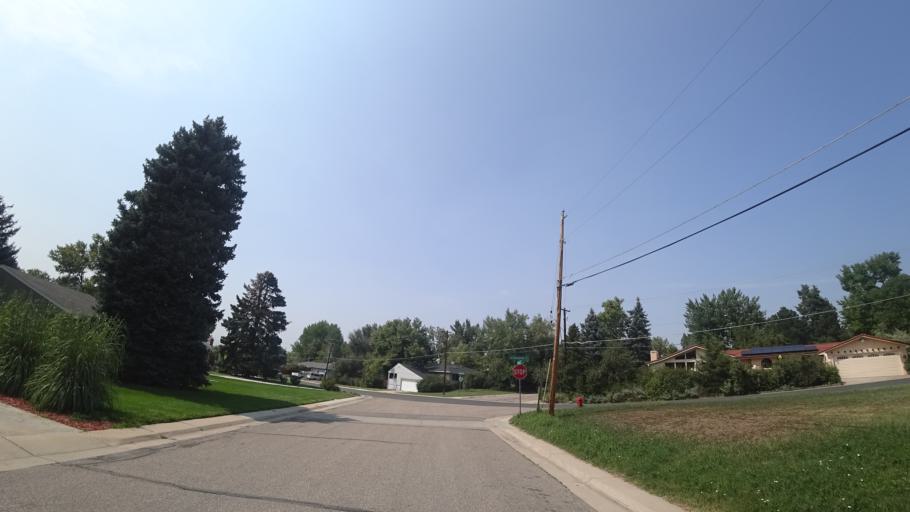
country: US
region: Colorado
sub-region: Arapahoe County
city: Littleton
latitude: 39.6274
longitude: -105.0005
